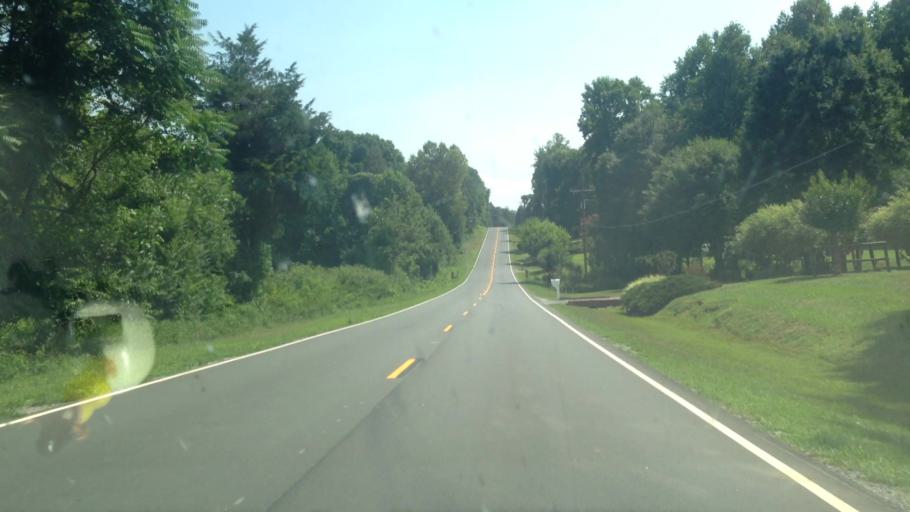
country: US
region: North Carolina
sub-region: Rockingham County
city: Mayodan
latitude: 36.4176
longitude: -80.0854
